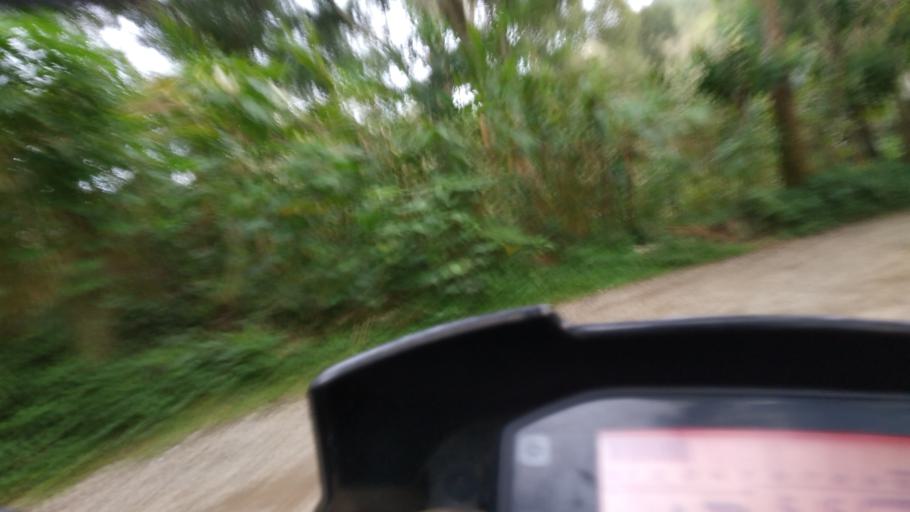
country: IN
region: Tamil Nadu
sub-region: Theni
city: Bodinayakkanur
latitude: 10.0239
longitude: 77.2484
